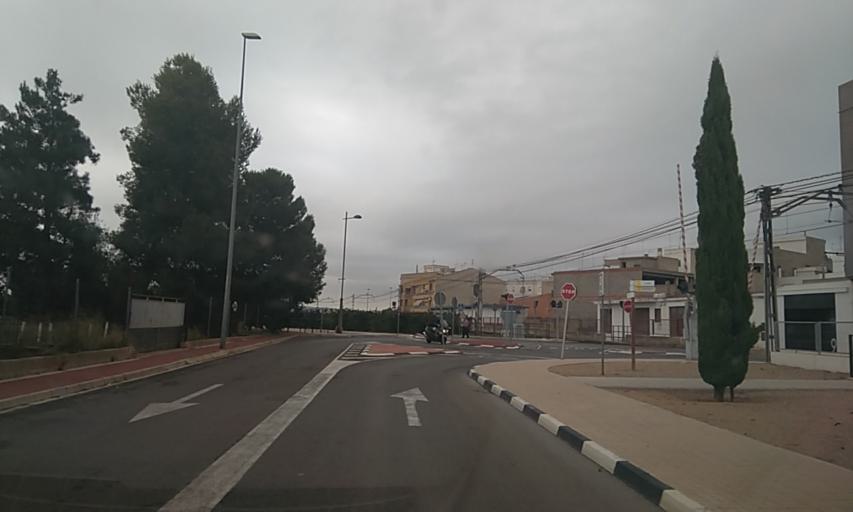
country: ES
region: Valencia
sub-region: Provincia de Valencia
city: L'Alcudia
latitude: 39.1990
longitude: -0.5098
